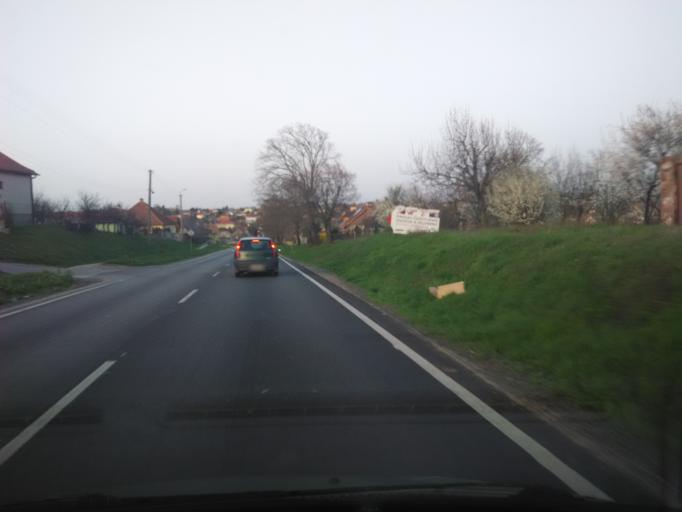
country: SK
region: Nitriansky
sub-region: Okres Nitra
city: Nitra
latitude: 48.2496
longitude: 18.0266
